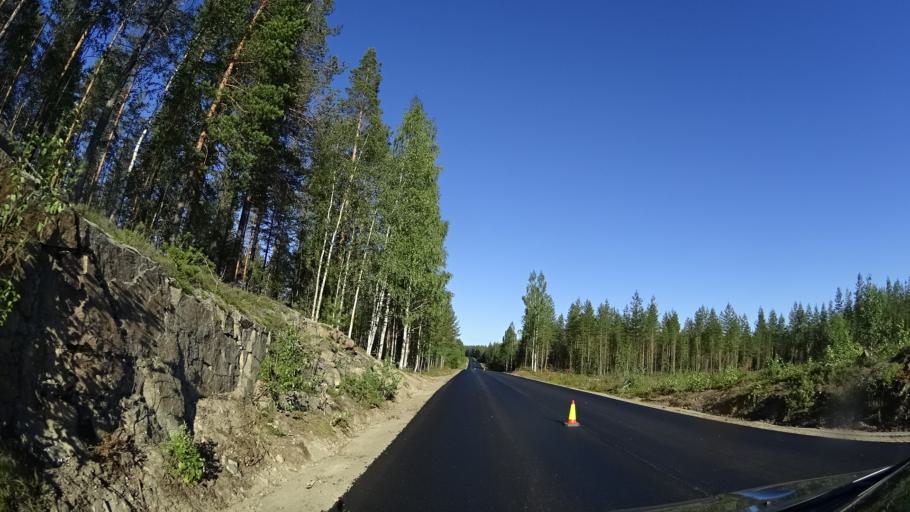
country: FI
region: North Karelia
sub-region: Pielisen Karjala
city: Valtimo
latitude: 63.5623
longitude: 28.5872
